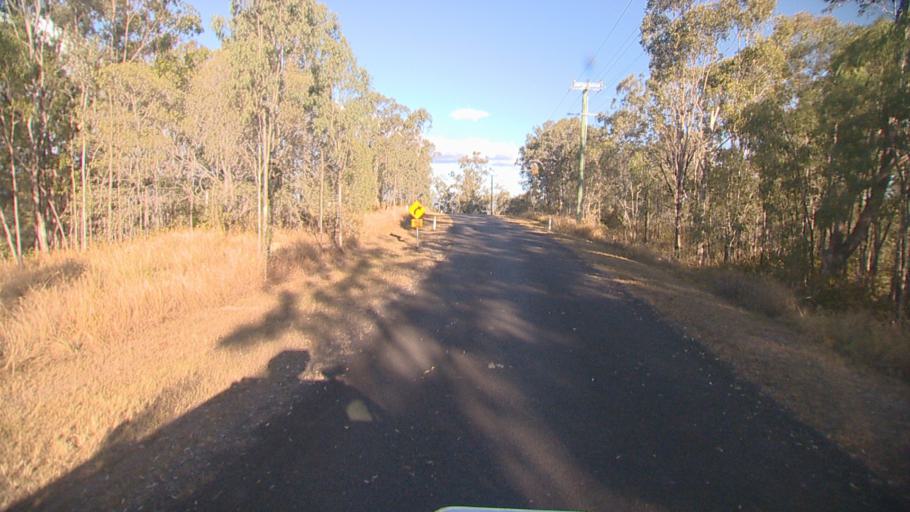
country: AU
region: Queensland
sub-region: Logan
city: Cedar Vale
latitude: -27.9200
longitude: 153.0657
